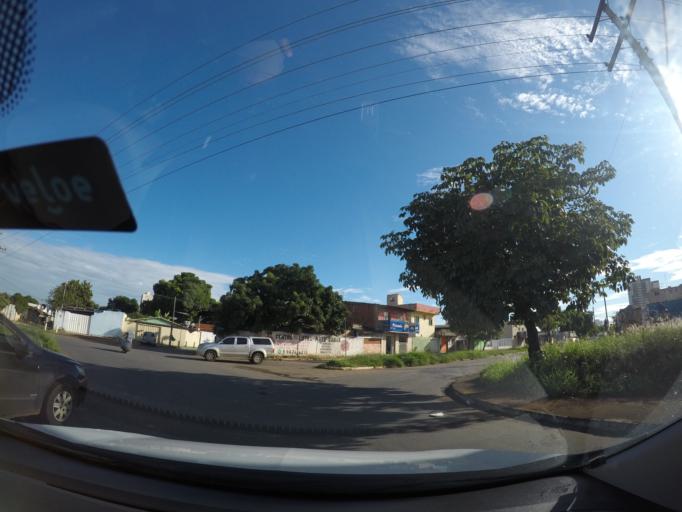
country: BR
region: Goias
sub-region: Goiania
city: Goiania
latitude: -16.7335
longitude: -49.2878
